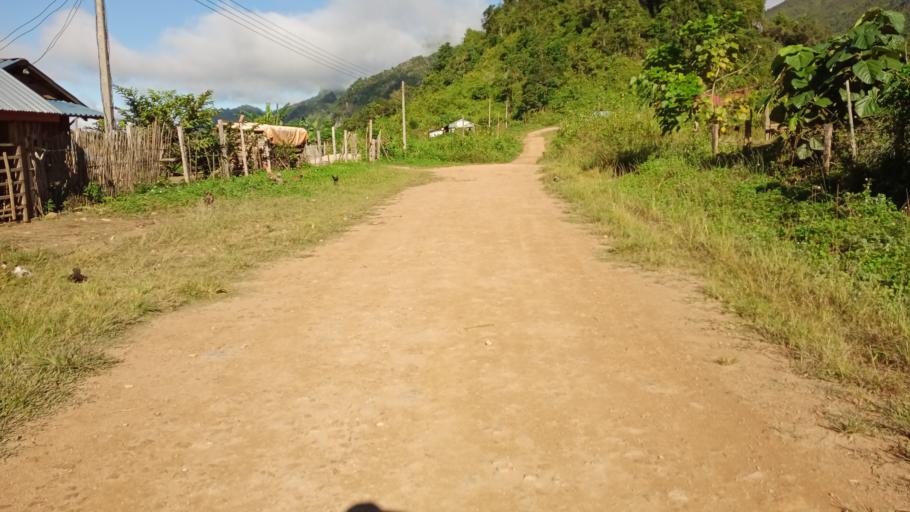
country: LA
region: Xiangkhoang
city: Phonsavan
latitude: 19.1161
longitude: 102.9107
